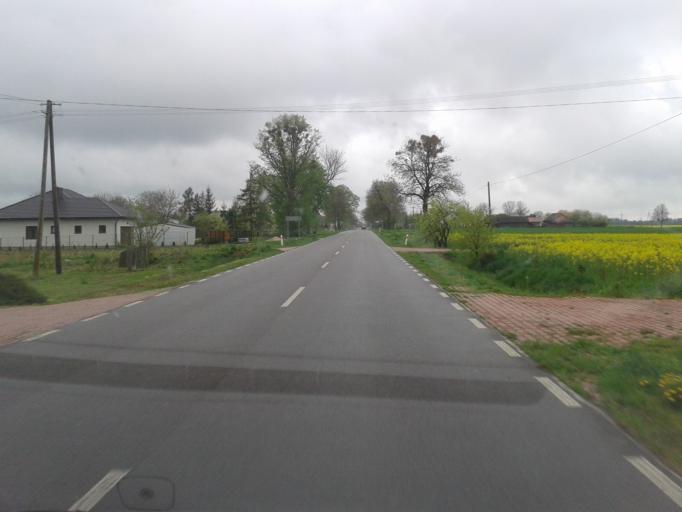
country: PL
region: Lublin Voivodeship
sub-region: Powiat hrubieszowski
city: Dolhobyczow
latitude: 50.5887
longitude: 23.9816
